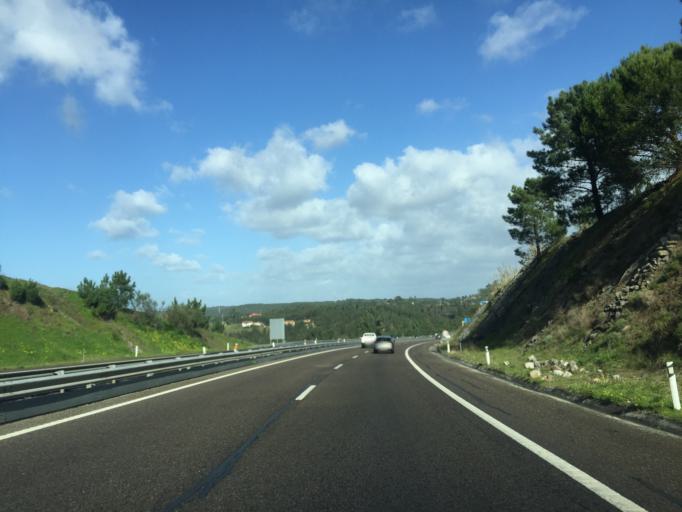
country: PT
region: Lisbon
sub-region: Torres Vedras
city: Torres Vedras
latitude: 39.0970
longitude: -9.2401
